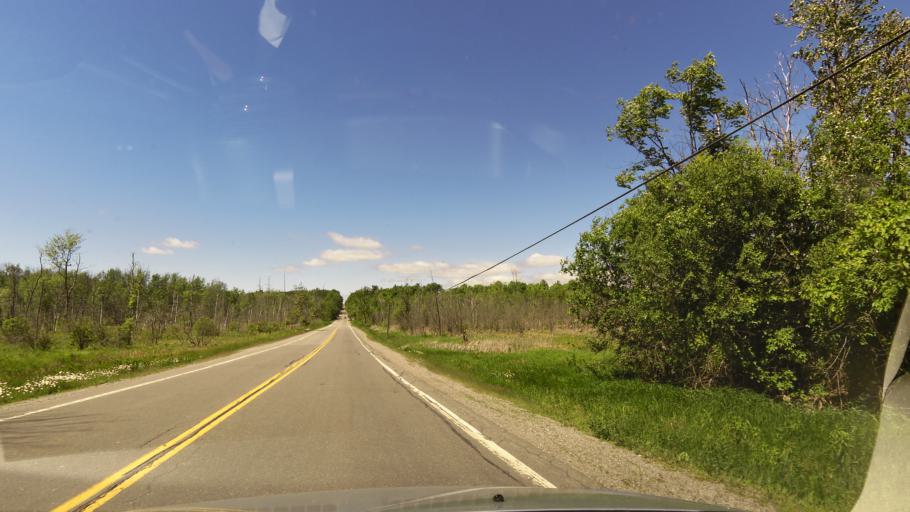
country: CA
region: Ontario
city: Vaughan
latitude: 43.9505
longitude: -79.5342
